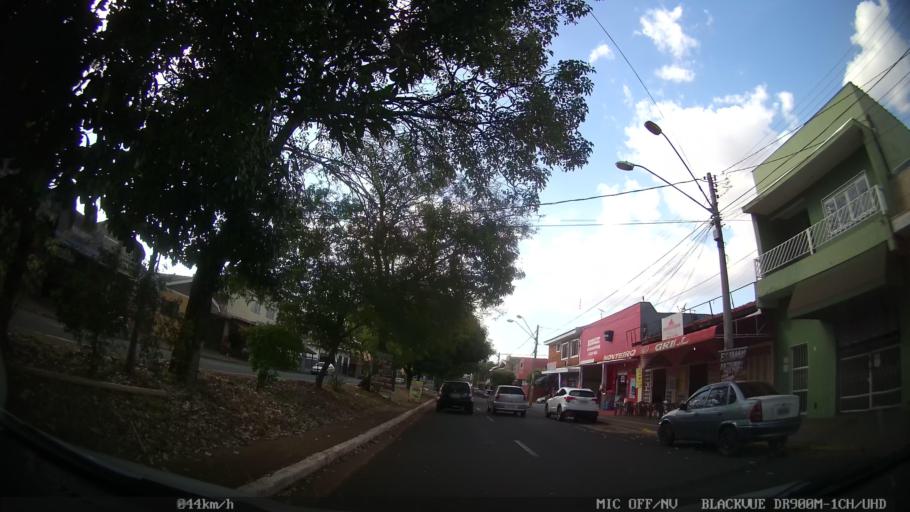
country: BR
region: Sao Paulo
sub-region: Ribeirao Preto
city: Ribeirao Preto
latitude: -21.1951
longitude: -47.8391
